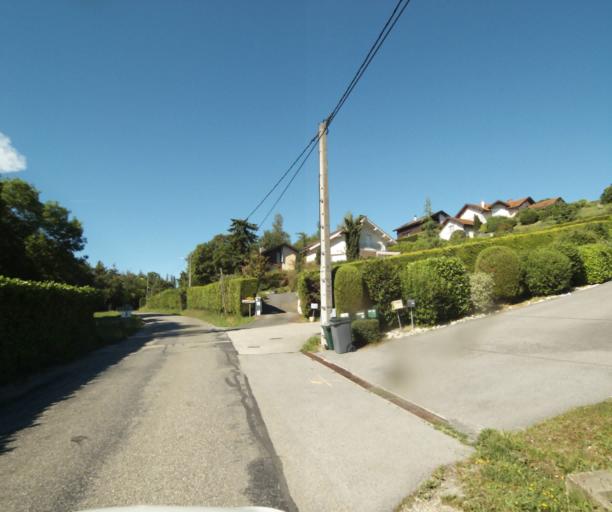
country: FR
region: Rhone-Alpes
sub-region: Departement de la Haute-Savoie
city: Ballaison
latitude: 46.3010
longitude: 6.3303
